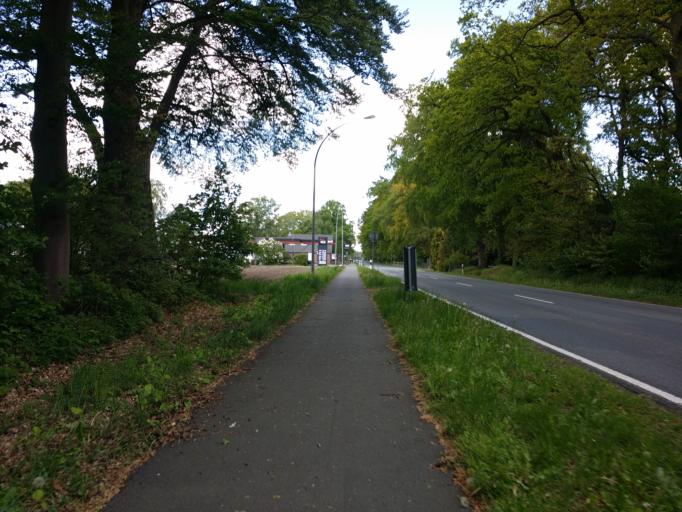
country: DE
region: Lower Saxony
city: Gross Ippener
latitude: 53.0091
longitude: 8.6080
